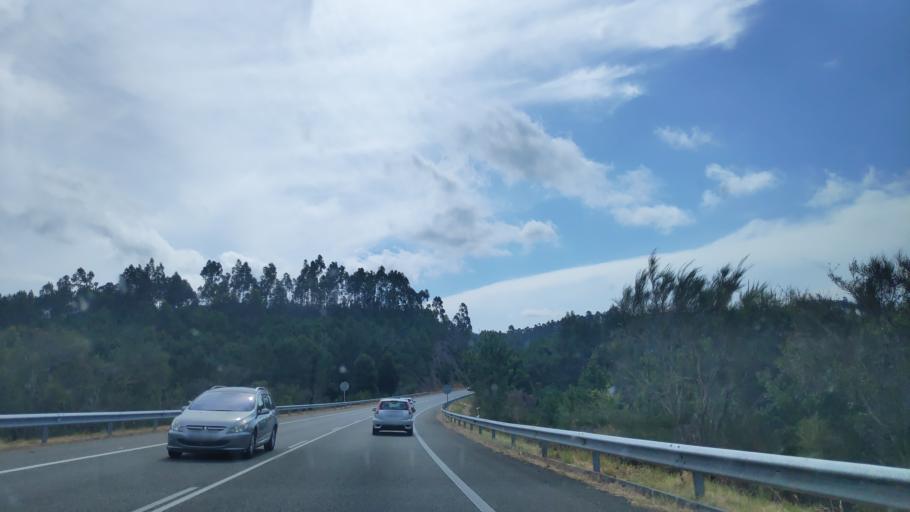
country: ES
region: Galicia
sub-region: Provincia de Pontevedra
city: Vilagarcia de Arousa
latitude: 42.6039
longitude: -8.7316
